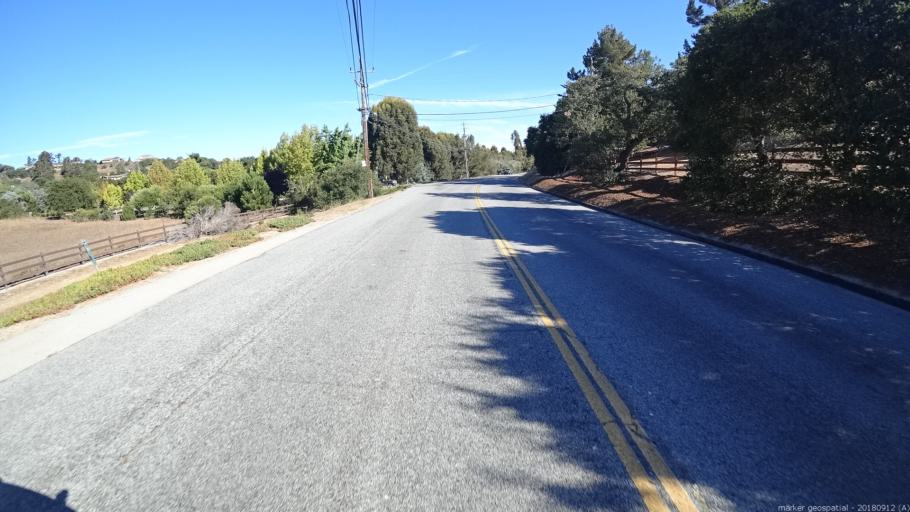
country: US
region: California
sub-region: Monterey County
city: Carmel Valley Village
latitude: 36.5618
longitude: -121.7326
